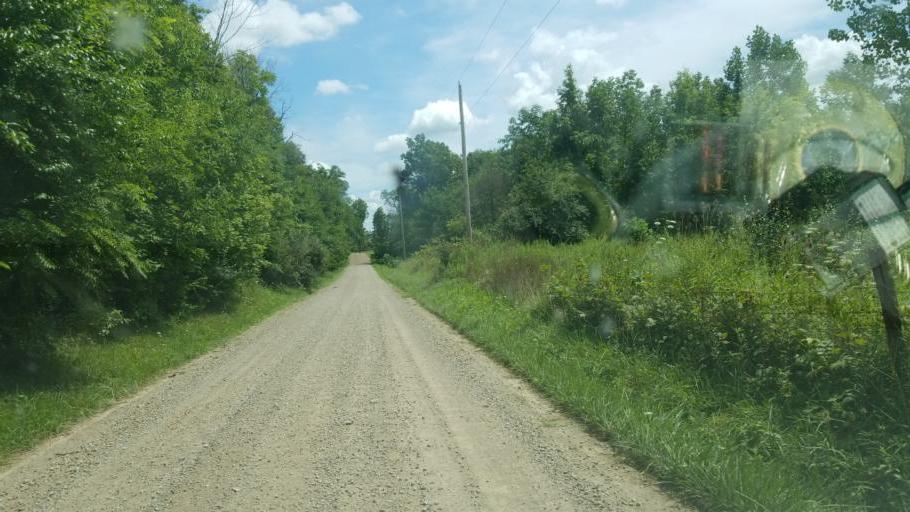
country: US
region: Ohio
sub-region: Knox County
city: Mount Vernon
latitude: 40.3678
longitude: -82.5897
